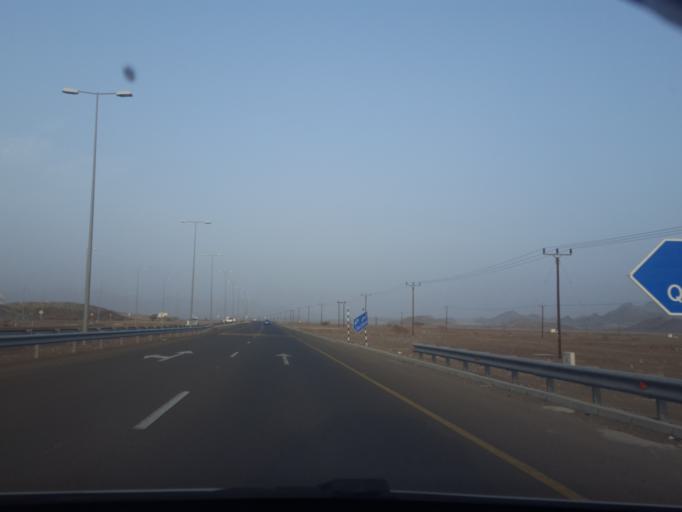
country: OM
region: Al Buraimi
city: Al Buraymi
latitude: 24.2467
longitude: 56.0178
